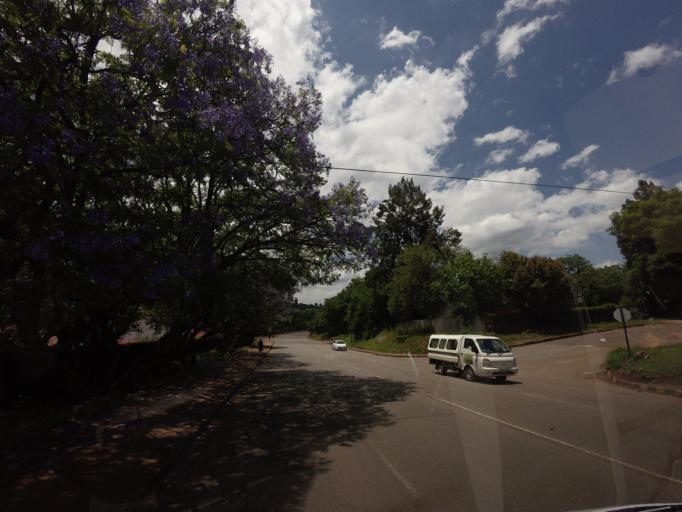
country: ZA
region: Mpumalanga
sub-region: Ehlanzeni District
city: Graksop
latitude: -25.0903
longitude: 30.7785
